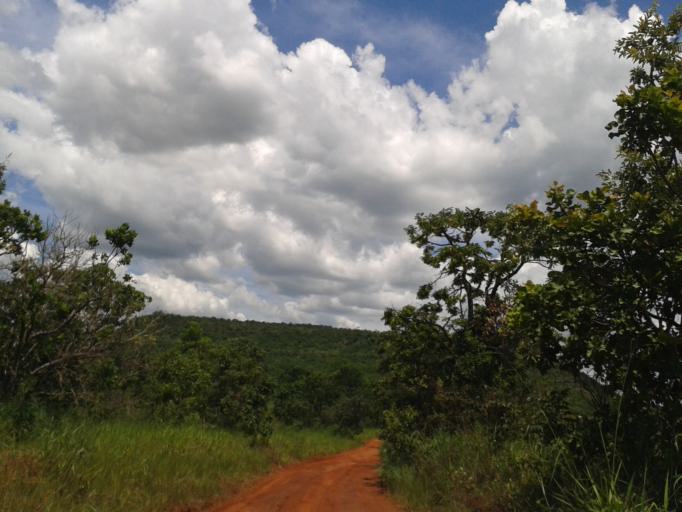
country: BR
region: Minas Gerais
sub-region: Ituiutaba
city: Ituiutaba
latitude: -18.8487
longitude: -49.5020
